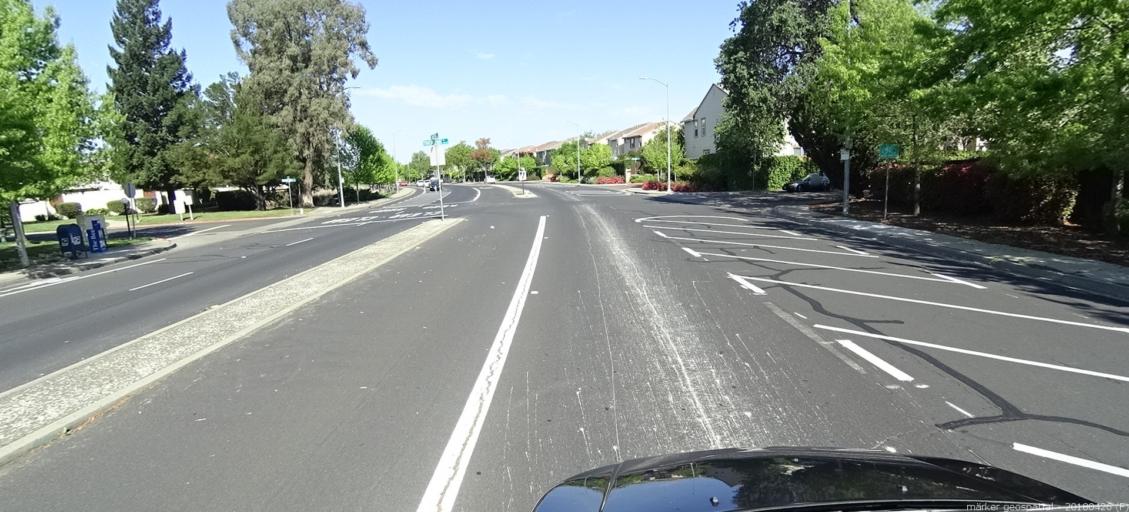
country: US
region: California
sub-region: Yolo County
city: West Sacramento
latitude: 38.5509
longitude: -121.5408
